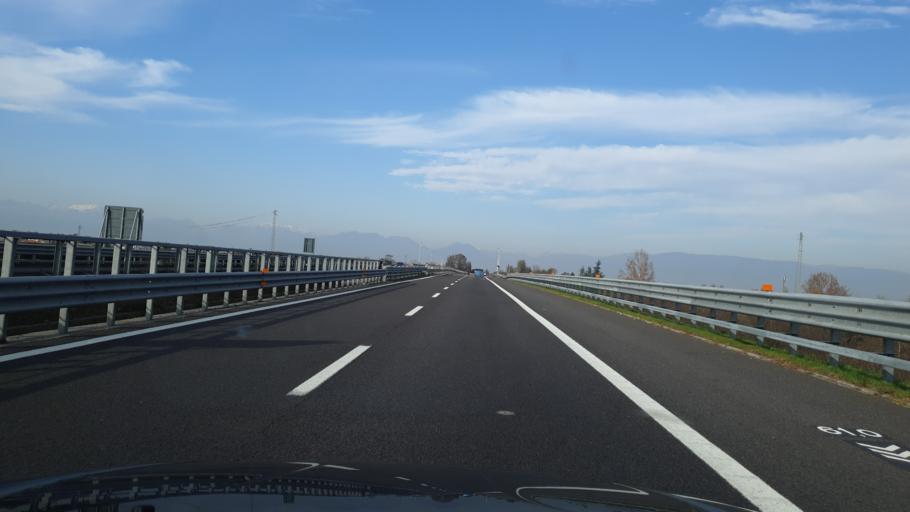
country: IT
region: Veneto
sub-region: Provincia di Vicenza
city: Lisiera
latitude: 45.5739
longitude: 11.6065
